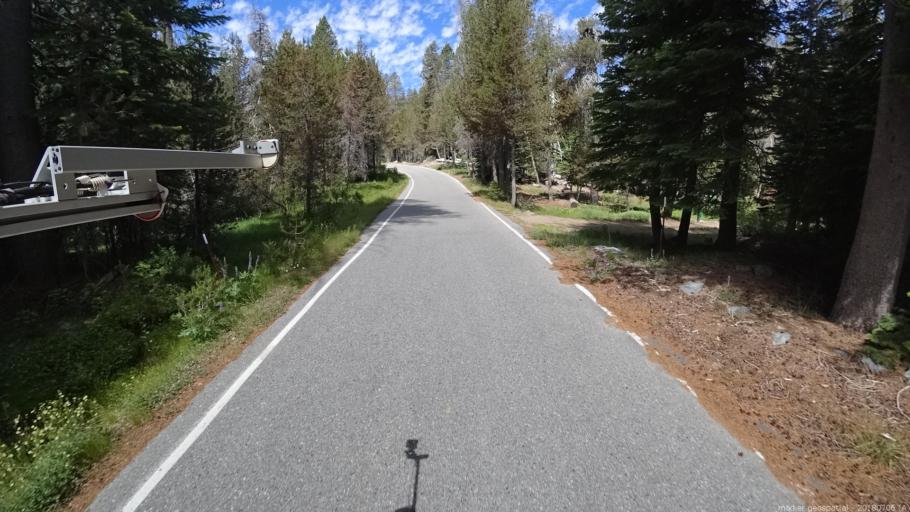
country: US
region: California
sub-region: Madera County
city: Oakhurst
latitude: 37.4454
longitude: -119.4624
